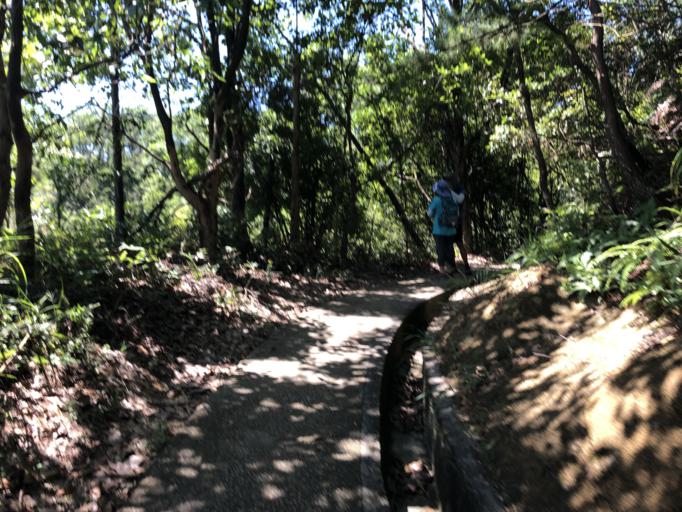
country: HK
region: Tuen Mun
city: Tuen Mun
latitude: 22.2794
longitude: 113.9872
